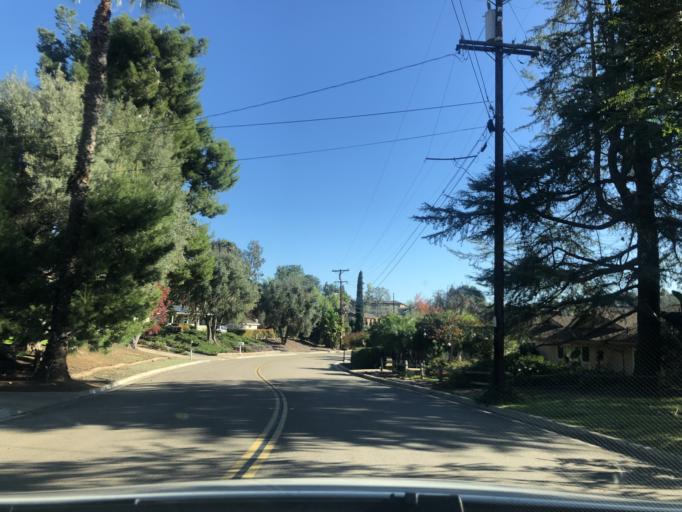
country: US
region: California
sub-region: San Diego County
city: Rancho San Diego
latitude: 32.7652
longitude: -116.9448
